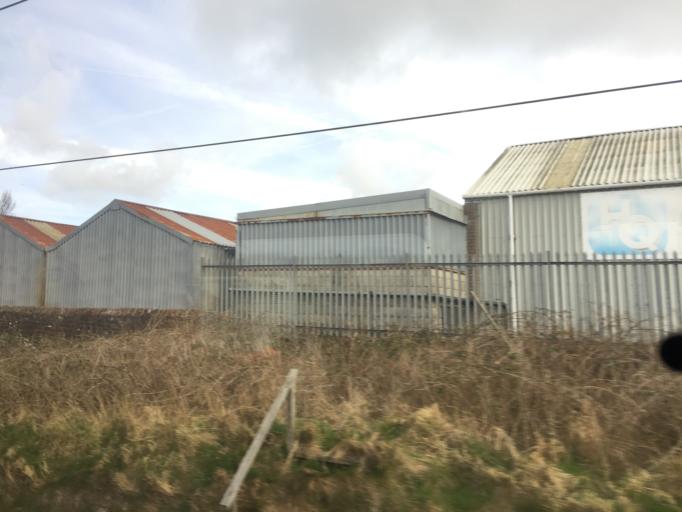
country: GB
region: England
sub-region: Cumbria
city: Penrith
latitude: 54.6686
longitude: -2.7615
